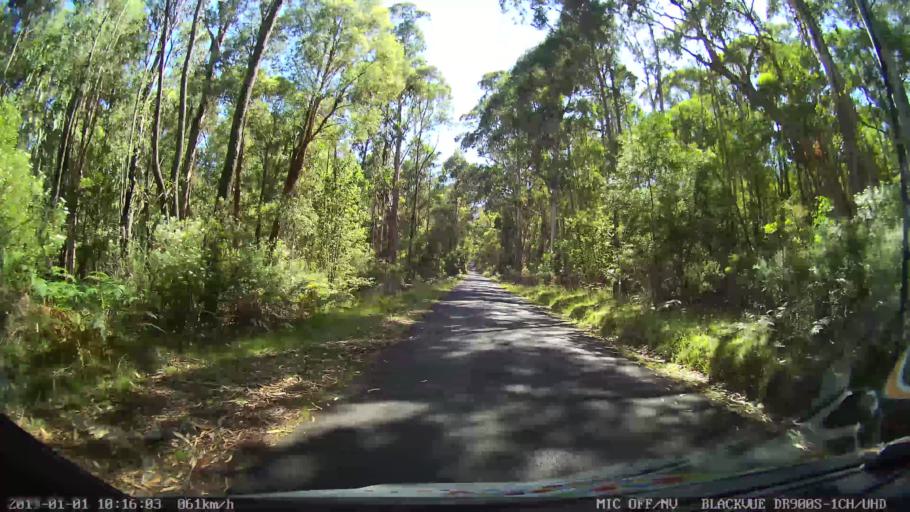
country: AU
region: New South Wales
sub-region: Snowy River
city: Jindabyne
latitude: -36.0962
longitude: 148.1641
